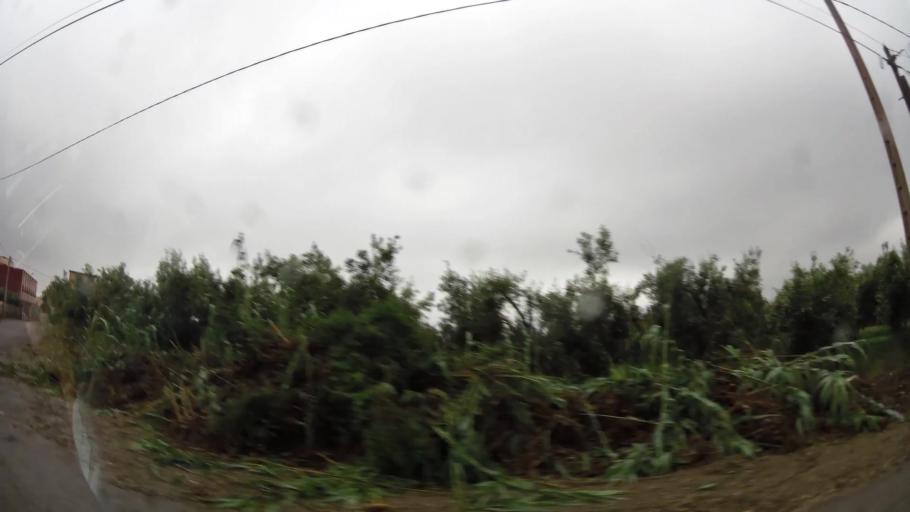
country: MA
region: Oriental
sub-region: Nador
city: Nador
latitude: 35.1529
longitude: -2.9677
